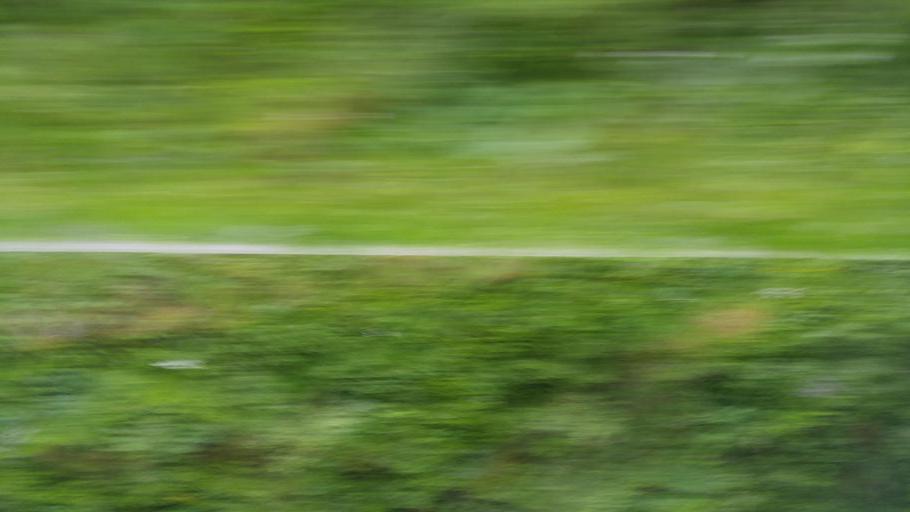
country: NO
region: Nord-Trondelag
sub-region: Meraker
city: Meraker
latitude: 63.4570
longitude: 11.4458
